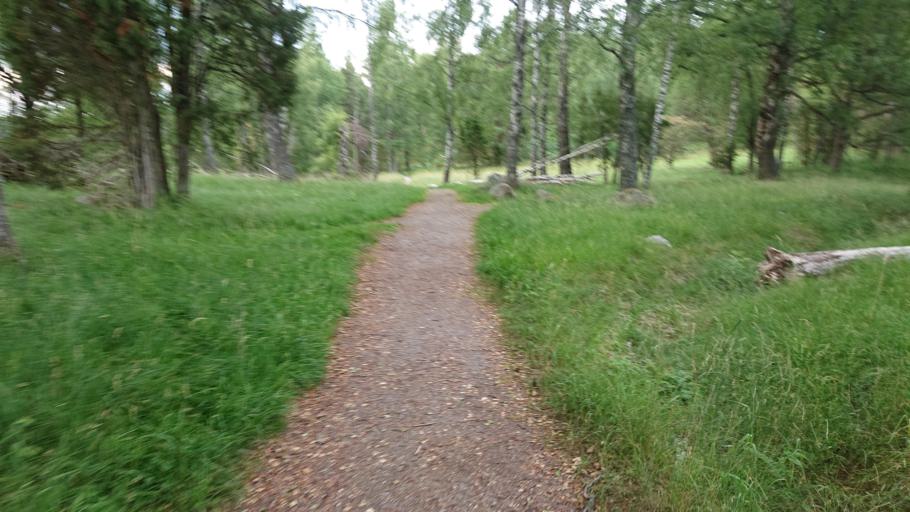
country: SE
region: Stockholm
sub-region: Osterakers Kommun
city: Akersberga
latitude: 59.4927
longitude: 18.2965
